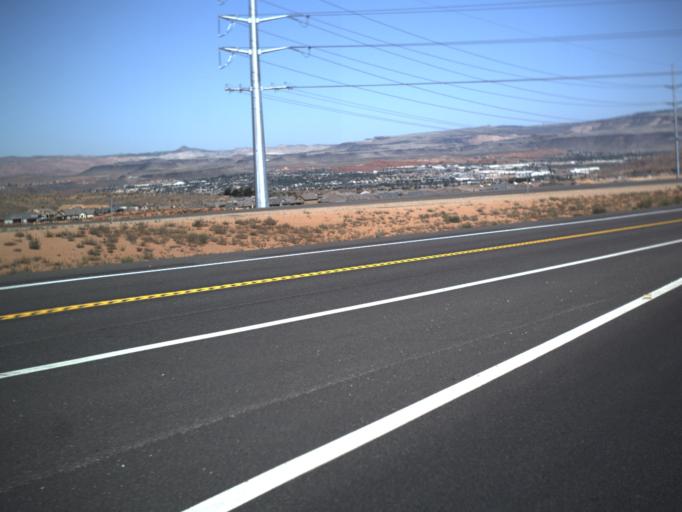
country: US
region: Utah
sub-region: Washington County
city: Washington
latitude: 37.0620
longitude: -113.4860
